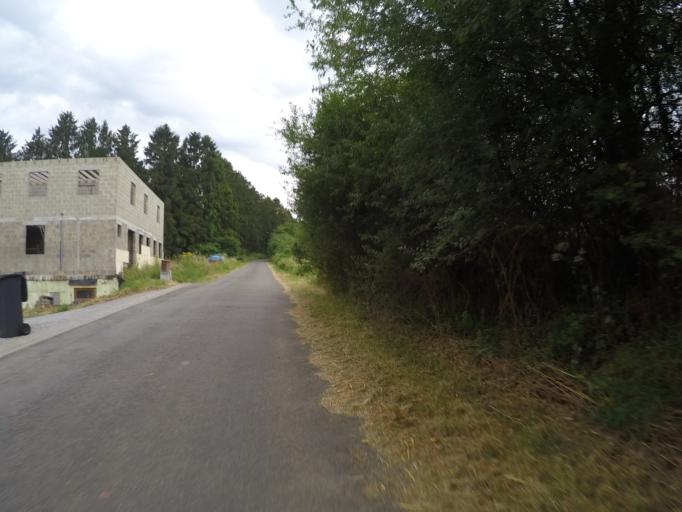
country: BE
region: Wallonia
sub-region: Province de Namur
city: Assesse
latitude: 50.3195
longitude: 5.0072
